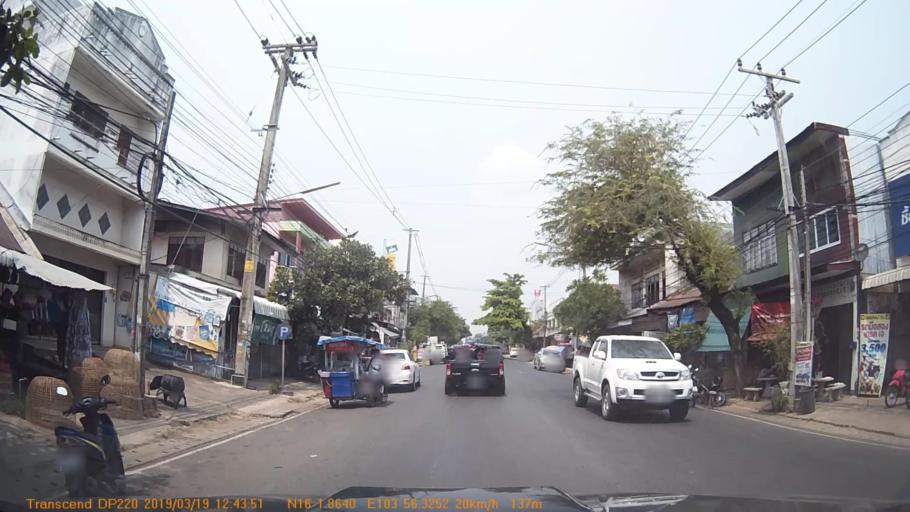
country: TH
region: Roi Et
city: Selaphum
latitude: 16.0310
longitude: 103.9388
